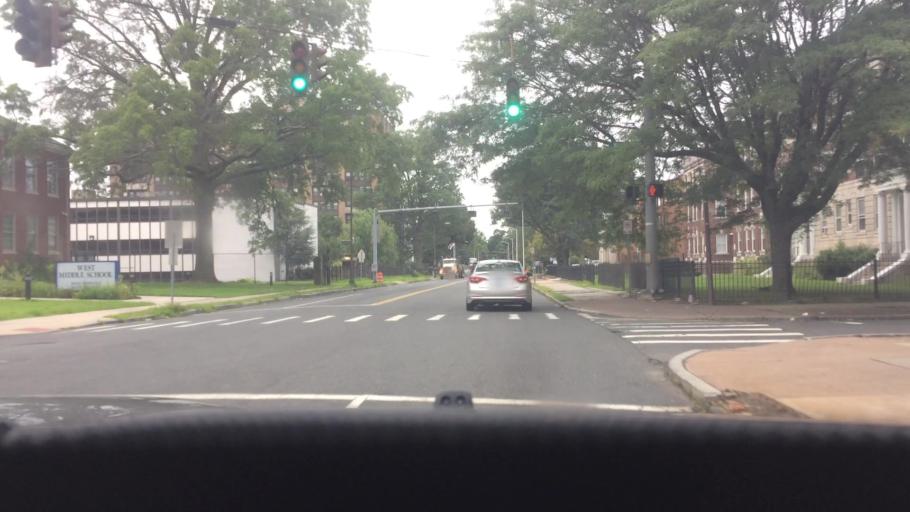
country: US
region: Connecticut
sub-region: Hartford County
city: Hartford
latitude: 41.7707
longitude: -72.6951
